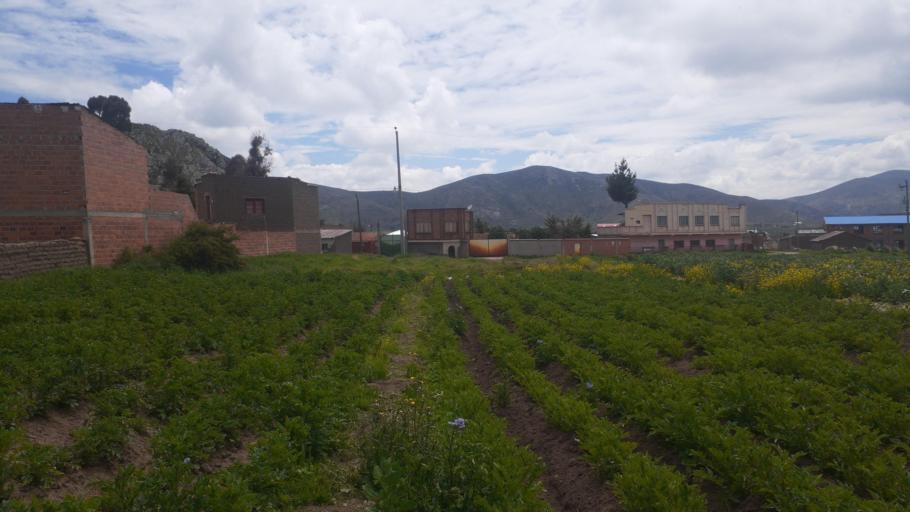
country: BO
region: La Paz
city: Batallas
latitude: -16.3479
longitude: -68.6382
